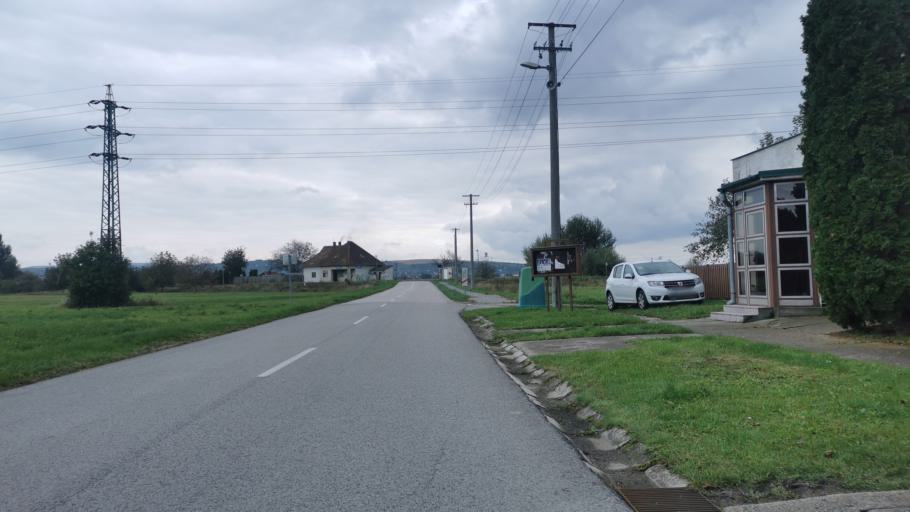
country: SK
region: Trnavsky
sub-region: Okres Skalica
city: Holic
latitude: 48.8289
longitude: 17.1757
